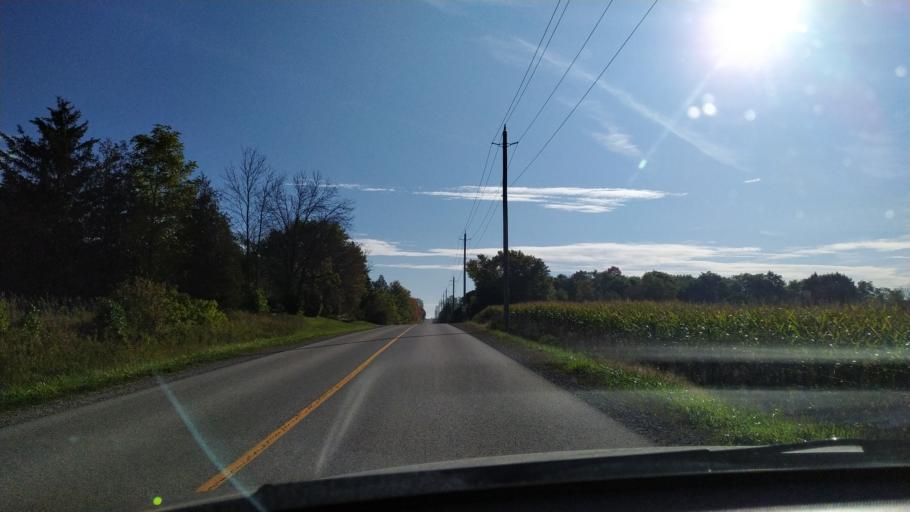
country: CA
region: Ontario
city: Stratford
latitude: 43.4958
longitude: -80.7607
